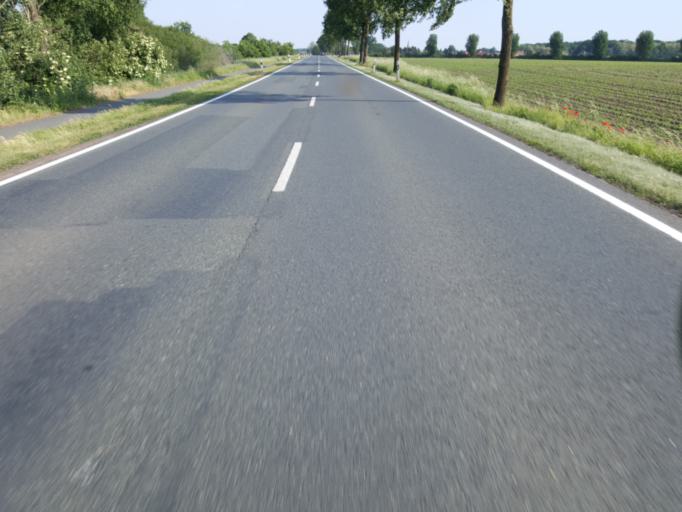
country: DE
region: Lower Saxony
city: Landesbergen
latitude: 52.5765
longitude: 9.1401
